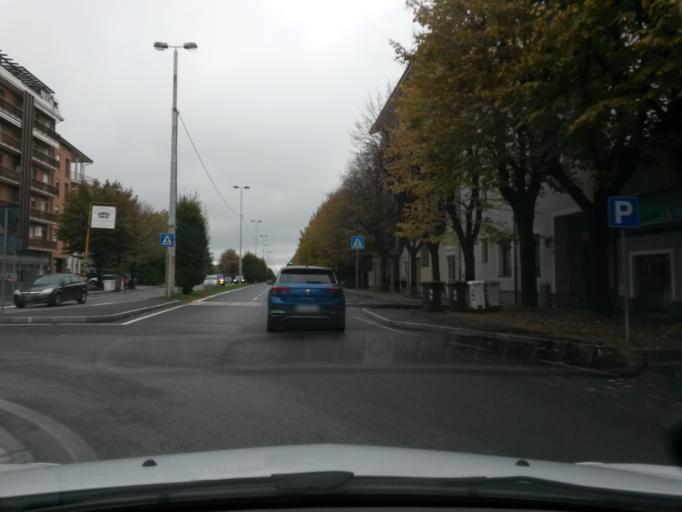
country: IT
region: Piedmont
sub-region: Provincia di Torino
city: Rivoli
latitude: 45.0703
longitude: 7.5217
